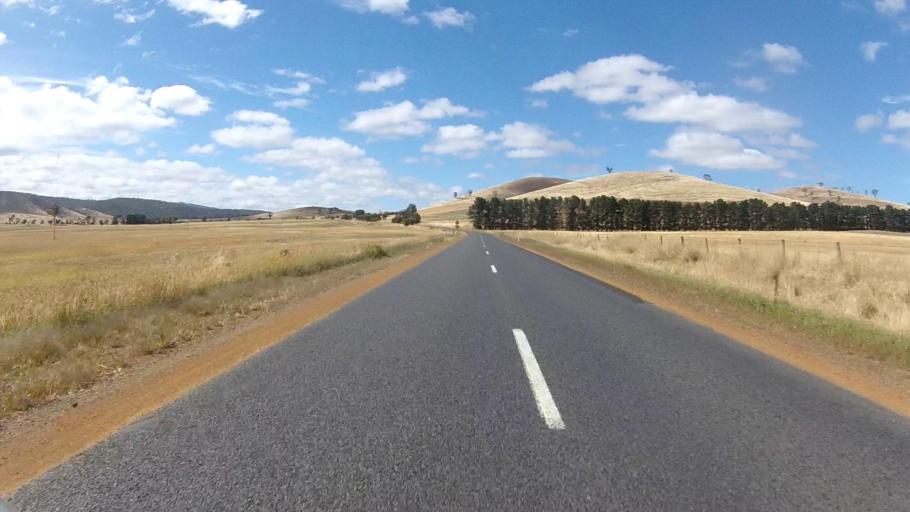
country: AU
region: Tasmania
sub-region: Brighton
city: Bridgewater
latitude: -42.5511
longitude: 147.3790
